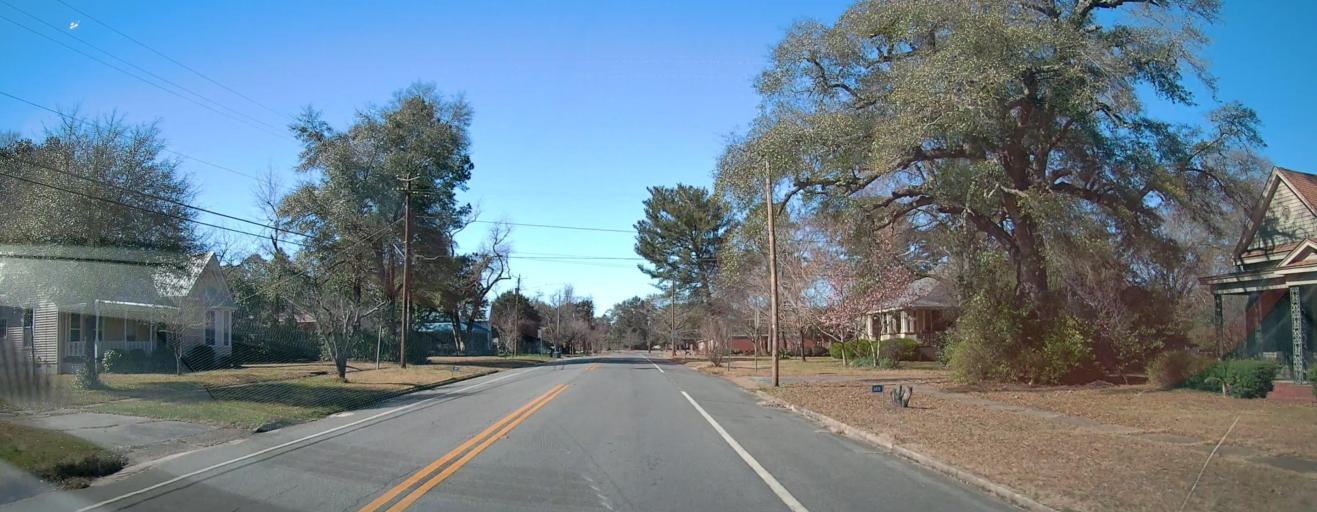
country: US
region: Georgia
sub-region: Macon County
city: Oglethorpe
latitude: 32.2972
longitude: -84.0640
